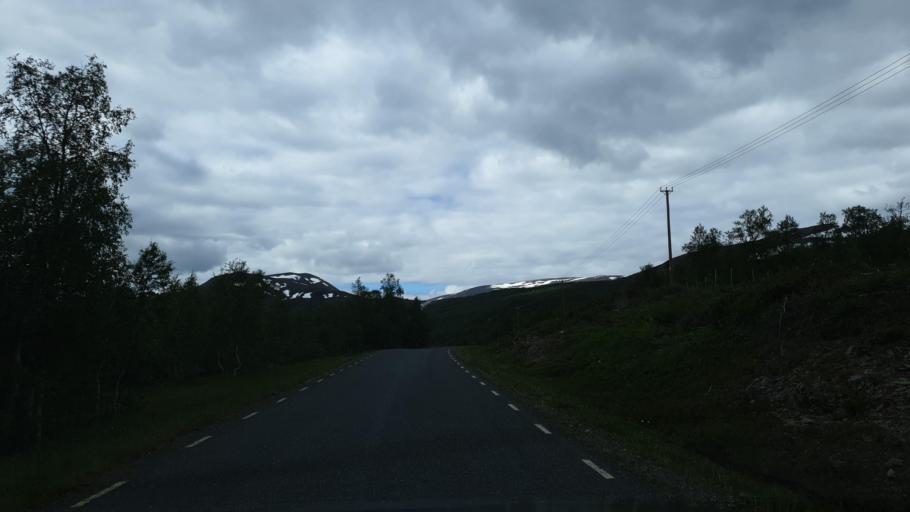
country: NO
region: Nordland
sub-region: Hattfjelldal
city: Hattfjelldal
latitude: 65.4195
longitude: 14.6778
